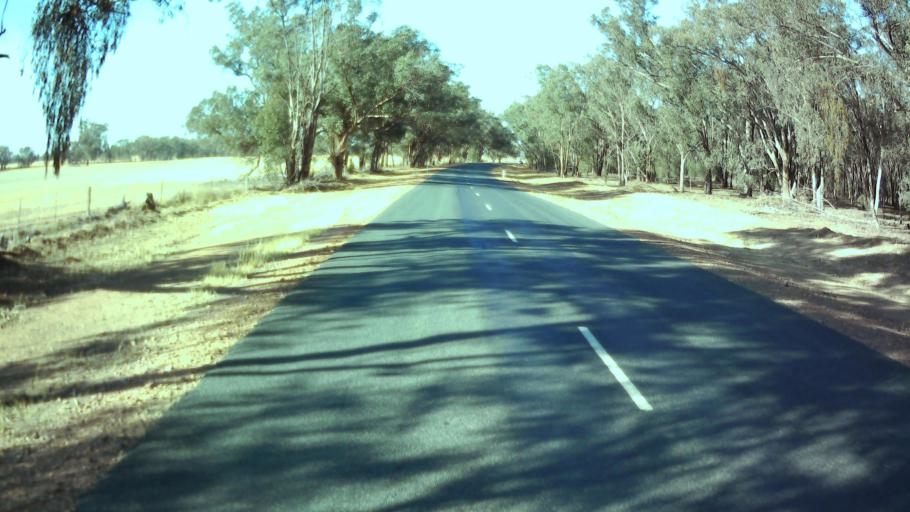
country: AU
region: New South Wales
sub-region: Weddin
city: Grenfell
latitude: -34.0073
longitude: 148.1222
